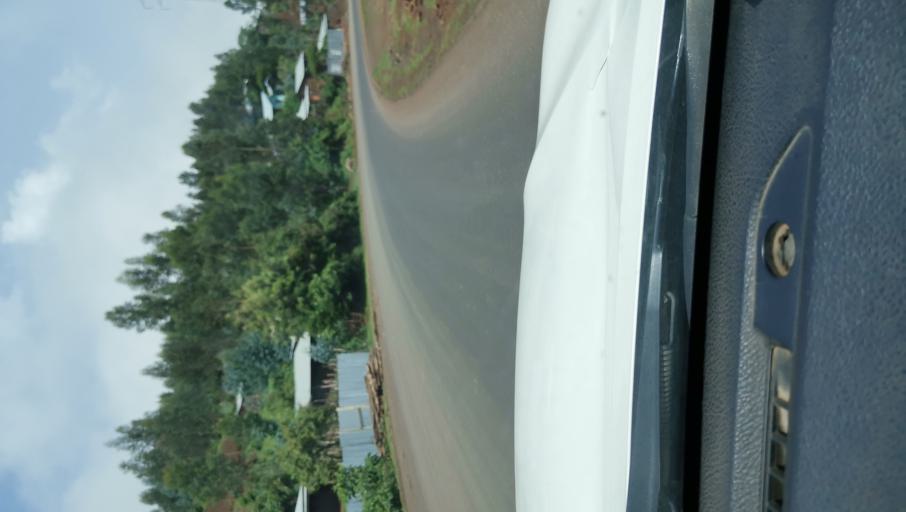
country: ET
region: Oromiya
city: Gedo
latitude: 9.0066
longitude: 37.4612
